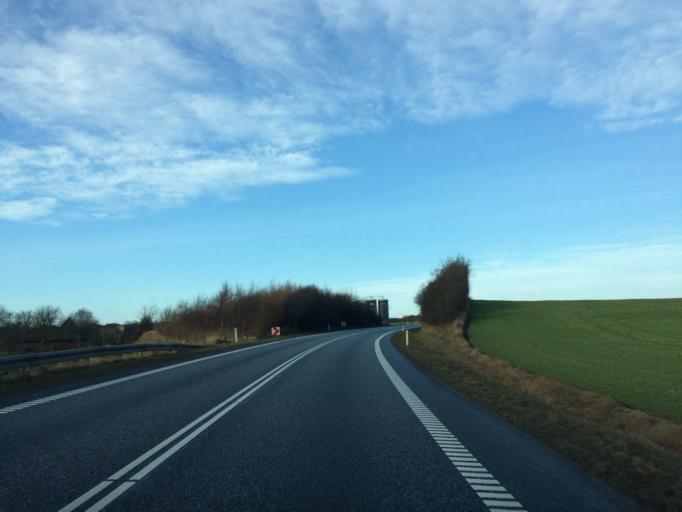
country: DK
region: Central Jutland
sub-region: Struer Kommune
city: Struer
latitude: 56.5074
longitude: 8.5715
